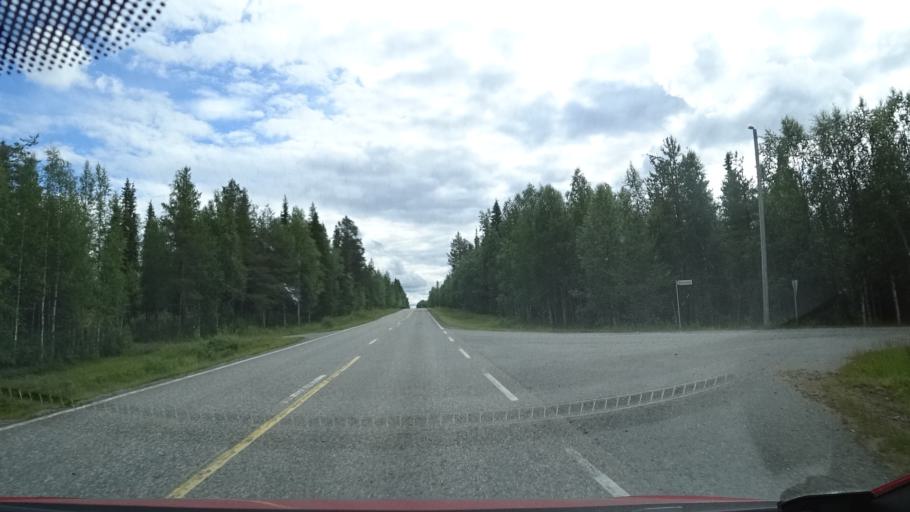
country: FI
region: Lapland
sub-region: Tunturi-Lappi
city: Kittilae
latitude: 67.4751
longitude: 24.9365
